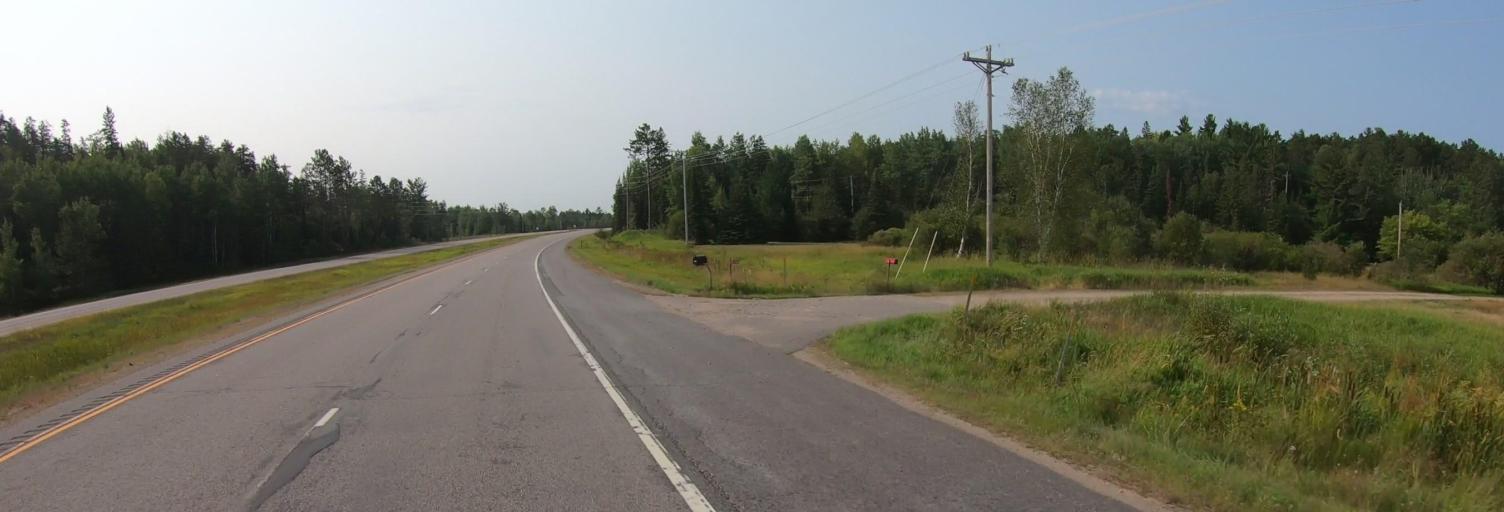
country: US
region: Minnesota
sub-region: Saint Louis County
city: Mountain Iron
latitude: 47.7080
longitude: -92.6456
